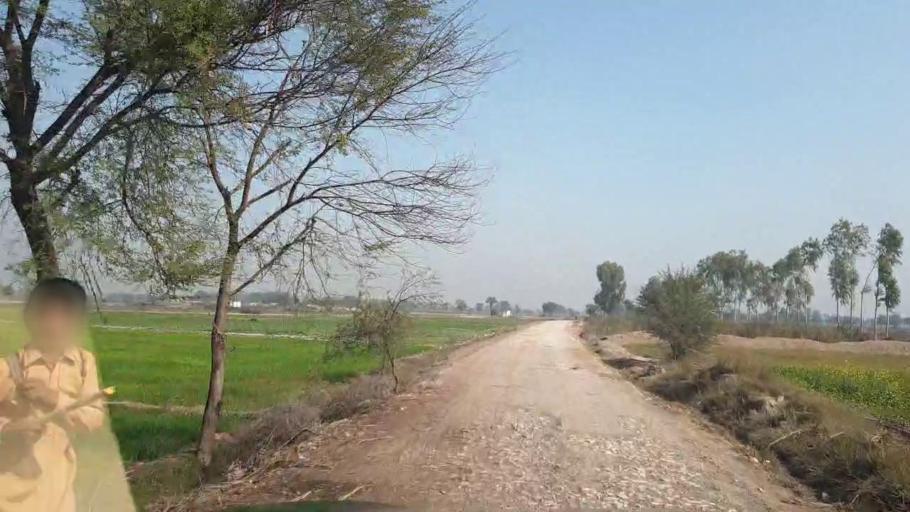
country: PK
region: Sindh
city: Ubauro
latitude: 28.1136
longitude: 69.7778
